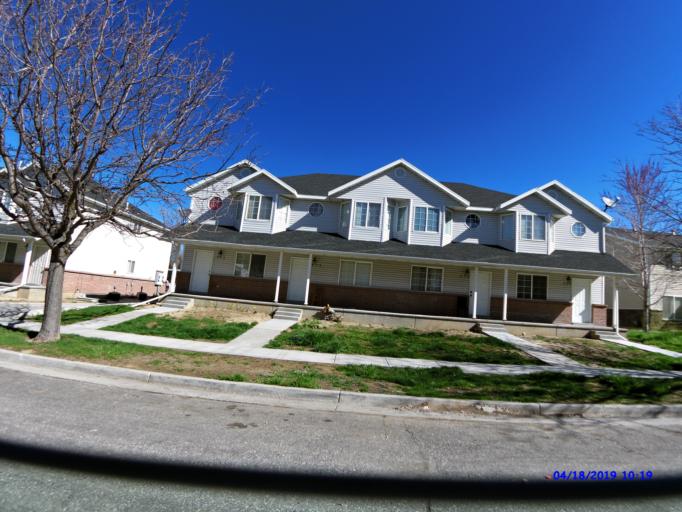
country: US
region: Utah
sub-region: Weber County
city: Harrisville
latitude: 41.2678
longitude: -111.9675
